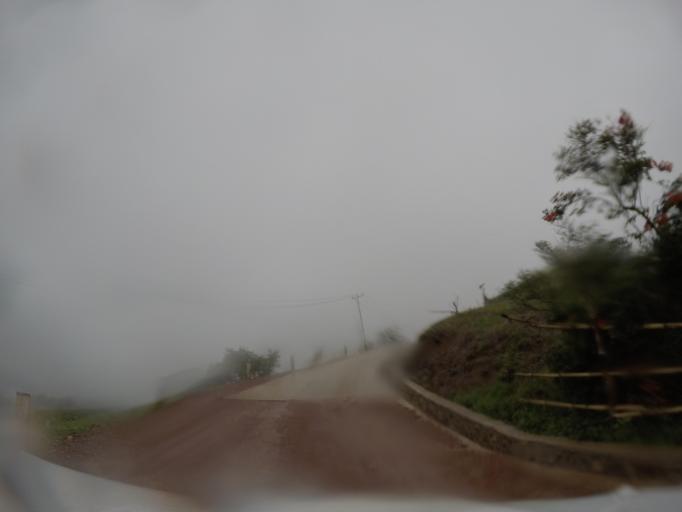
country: TL
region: Baucau
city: Venilale
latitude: -8.6383
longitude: 126.4078
